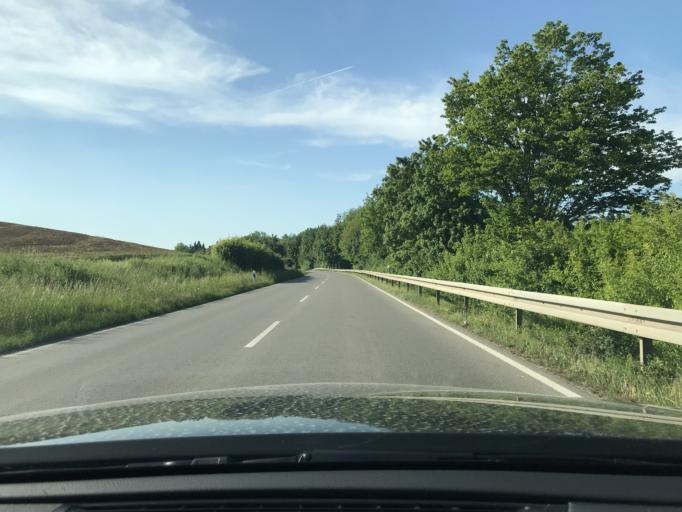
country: DE
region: Baden-Wuerttemberg
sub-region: Regierungsbezirk Stuttgart
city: Schwaikheim
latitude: 48.8800
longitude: 9.3179
